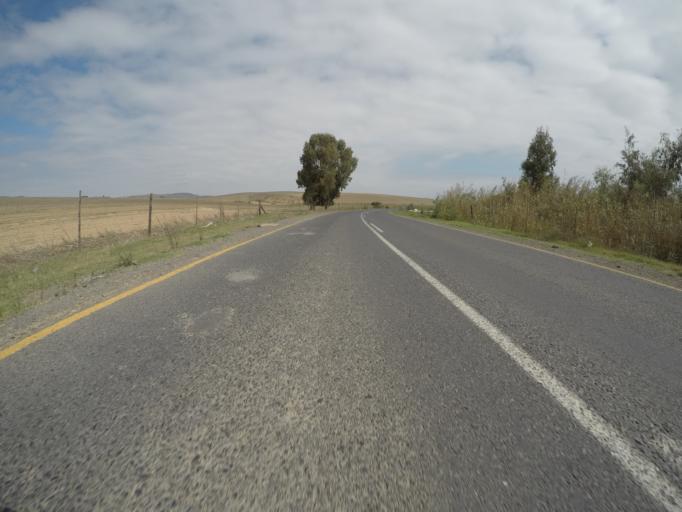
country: ZA
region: Western Cape
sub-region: City of Cape Town
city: Sunset Beach
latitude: -33.7868
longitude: 18.5551
